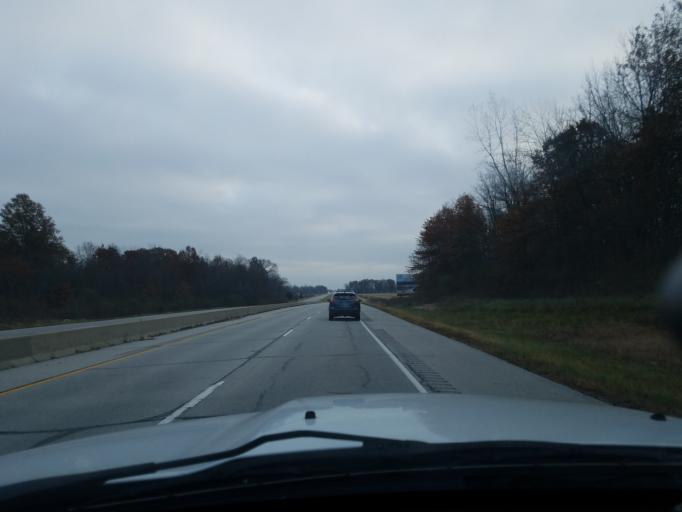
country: US
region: Indiana
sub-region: Delaware County
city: Yorktown
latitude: 40.2191
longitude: -85.5117
